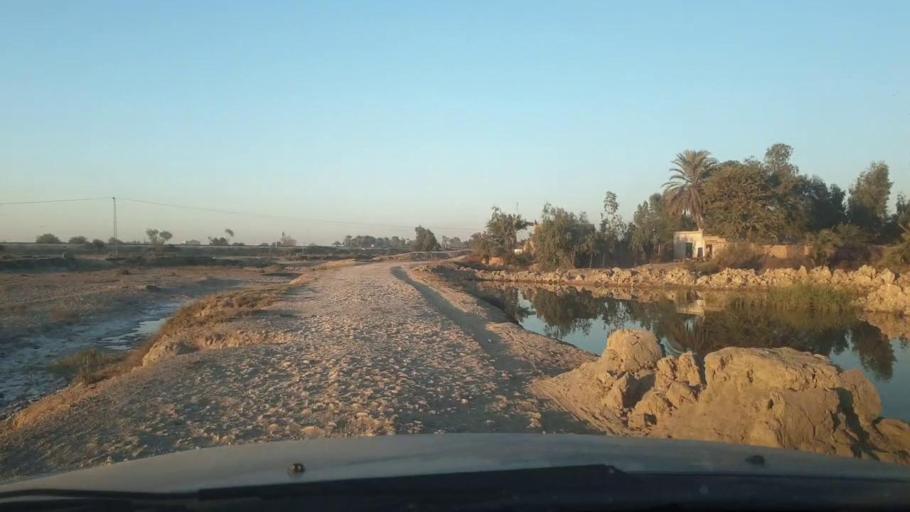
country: PK
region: Sindh
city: Pano Aqil
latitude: 27.9162
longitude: 69.1939
